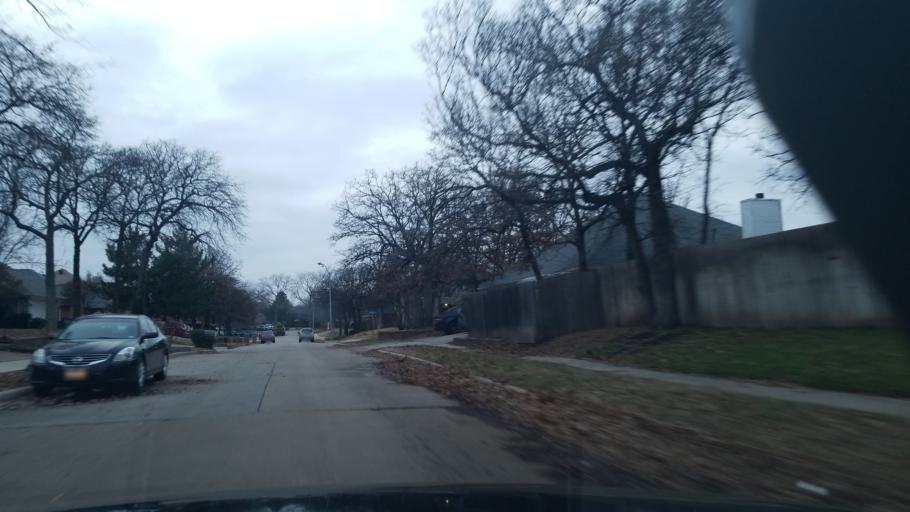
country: US
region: Texas
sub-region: Denton County
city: Corinth
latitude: 33.1358
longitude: -97.0716
